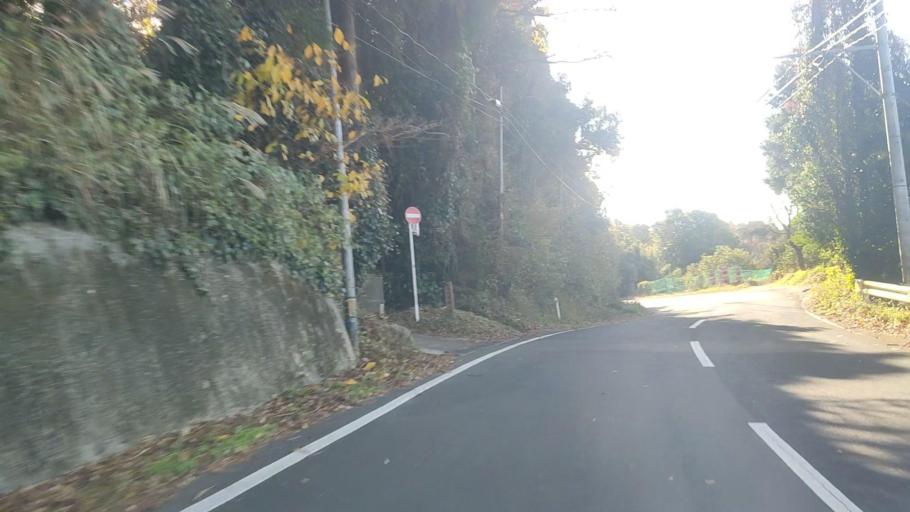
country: JP
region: Kagoshima
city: Kokubu-matsuki
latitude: 31.6678
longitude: 130.8224
